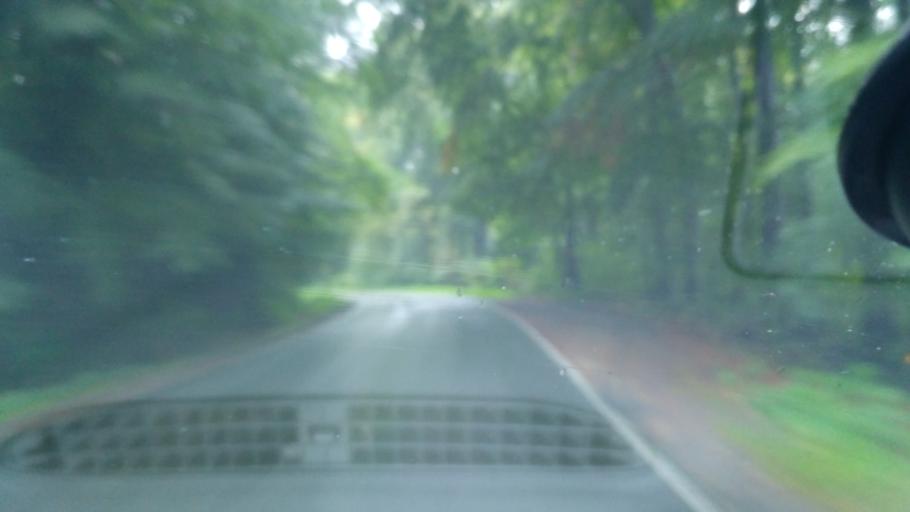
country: PL
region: Subcarpathian Voivodeship
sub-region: Powiat ropczycko-sedziszowski
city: Niedzwiada
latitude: 50.0574
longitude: 21.5356
